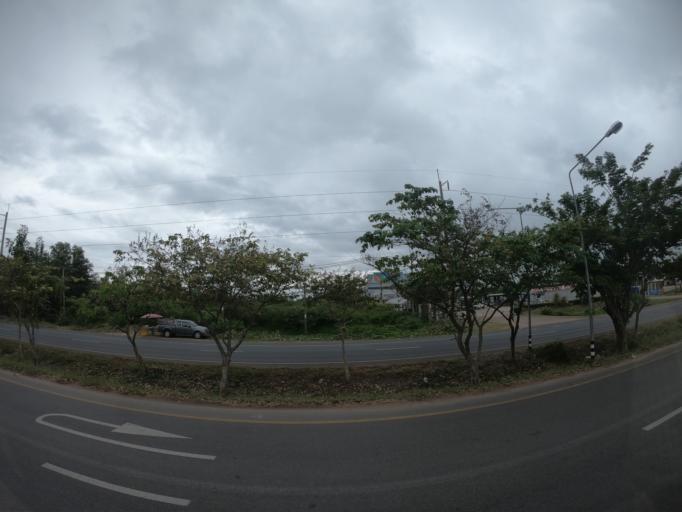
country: TH
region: Roi Et
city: Roi Et
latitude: 16.0539
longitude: 103.6202
